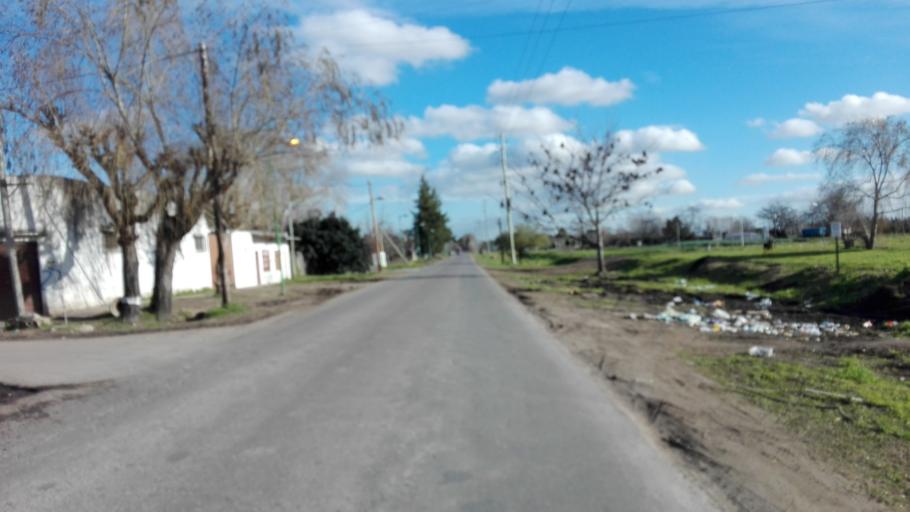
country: AR
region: Buenos Aires
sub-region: Partido de La Plata
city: La Plata
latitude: -34.9095
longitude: -58.0205
